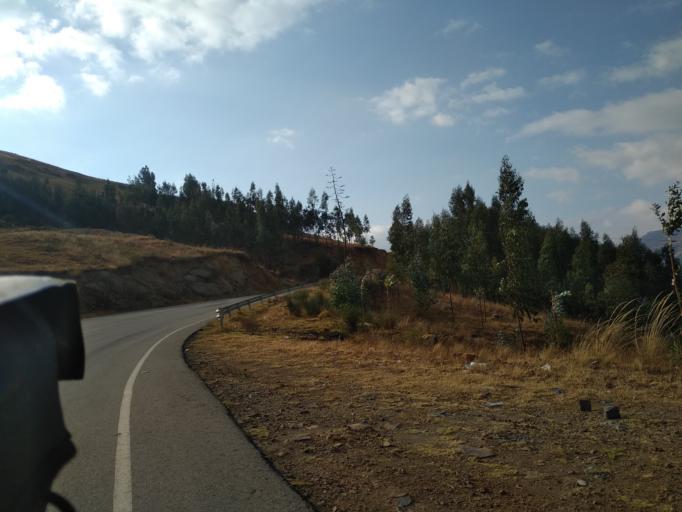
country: PE
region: La Libertad
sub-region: Provincia de Otuzco
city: Agallpampa
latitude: -7.9877
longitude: -78.5344
